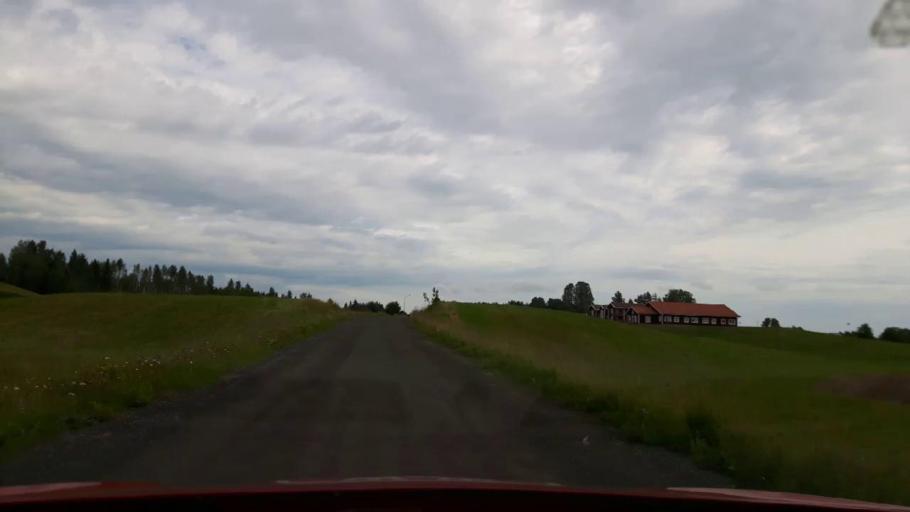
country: SE
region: Jaemtland
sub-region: OEstersunds Kommun
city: Lit
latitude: 63.4136
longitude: 15.2454
